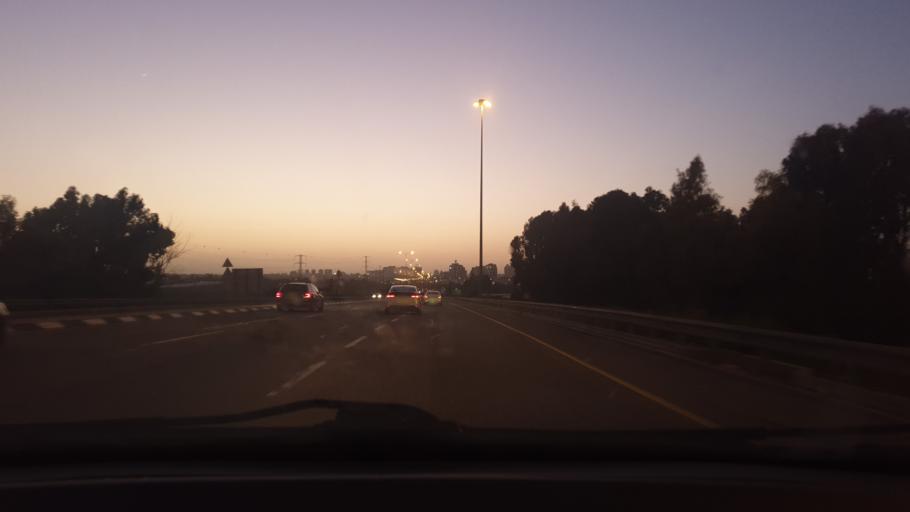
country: IL
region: Central District
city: Nehalim
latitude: 32.0681
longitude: 34.9326
